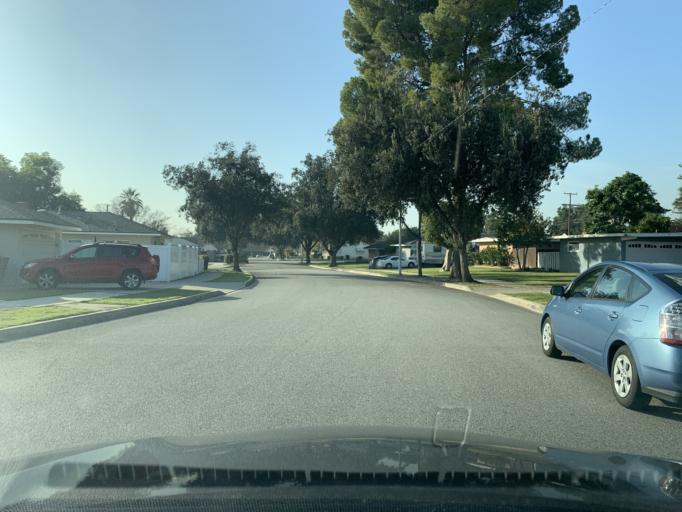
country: US
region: California
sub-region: Los Angeles County
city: Covina
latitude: 34.0840
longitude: -117.8956
